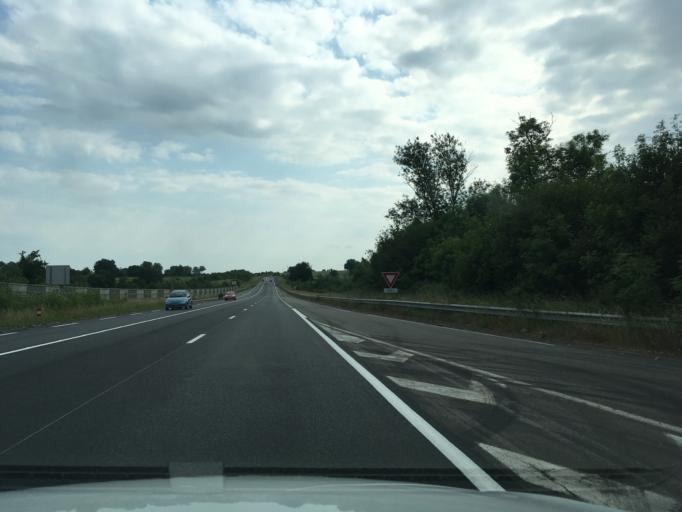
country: FR
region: Poitou-Charentes
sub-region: Departement des Deux-Sevres
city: Parthenay
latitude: 46.6512
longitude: -0.2702
